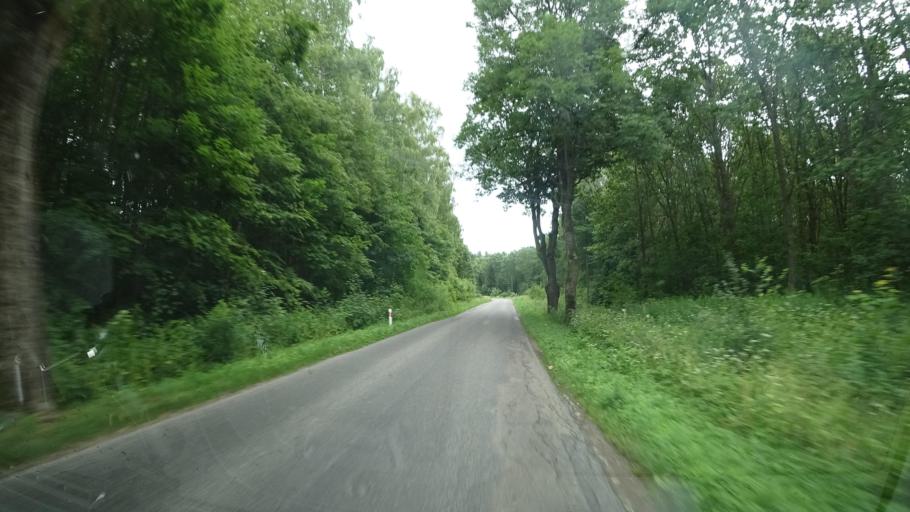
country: PL
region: Warmian-Masurian Voivodeship
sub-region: Powiat goldapski
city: Goldap
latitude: 54.3099
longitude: 22.3831
